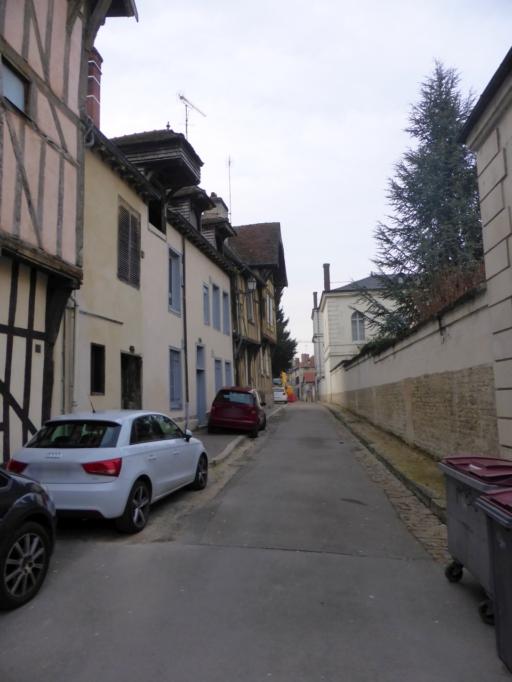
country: FR
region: Champagne-Ardenne
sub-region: Departement de l'Aube
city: Troyes
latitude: 48.3011
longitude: 4.0821
